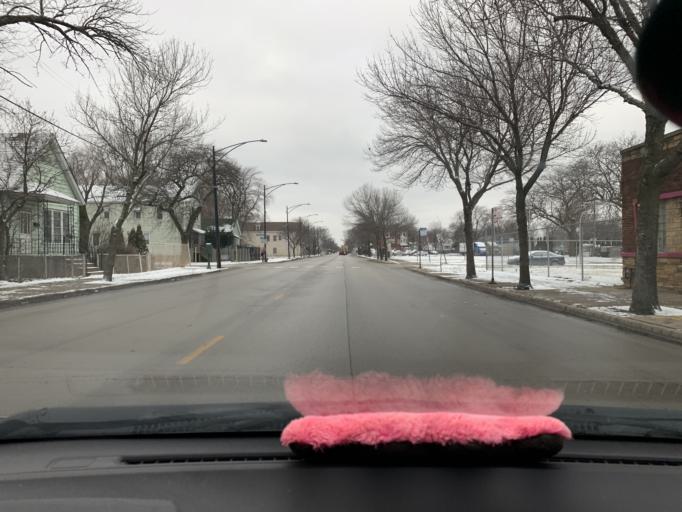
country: US
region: Illinois
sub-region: Cook County
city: Chicago
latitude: 41.8016
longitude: -87.6473
